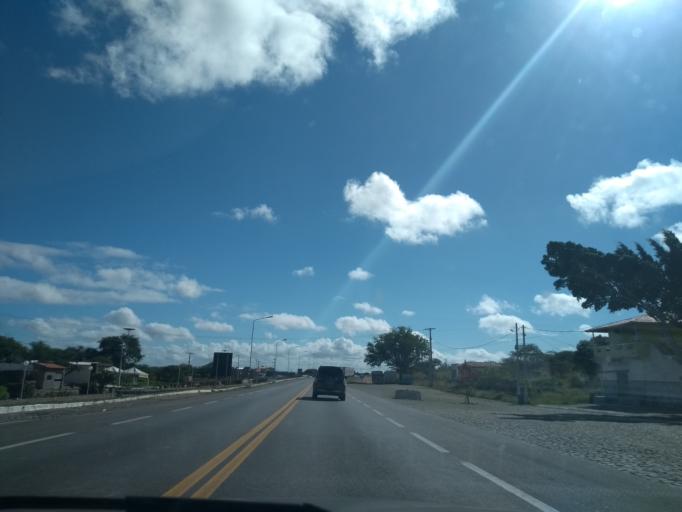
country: BR
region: Bahia
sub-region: Amargosa
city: Amargosa
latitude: -12.8689
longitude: -39.8558
